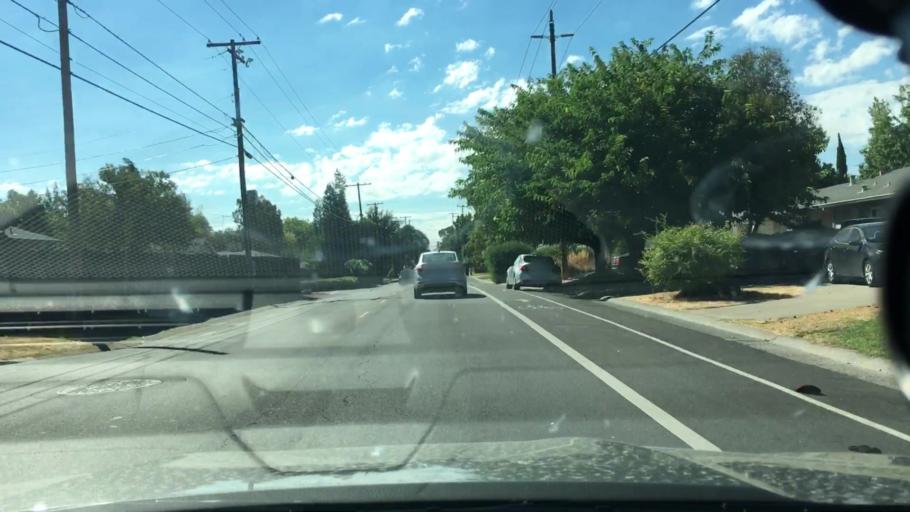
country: US
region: California
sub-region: Sacramento County
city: Arden-Arcade
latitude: 38.5914
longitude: -121.3923
